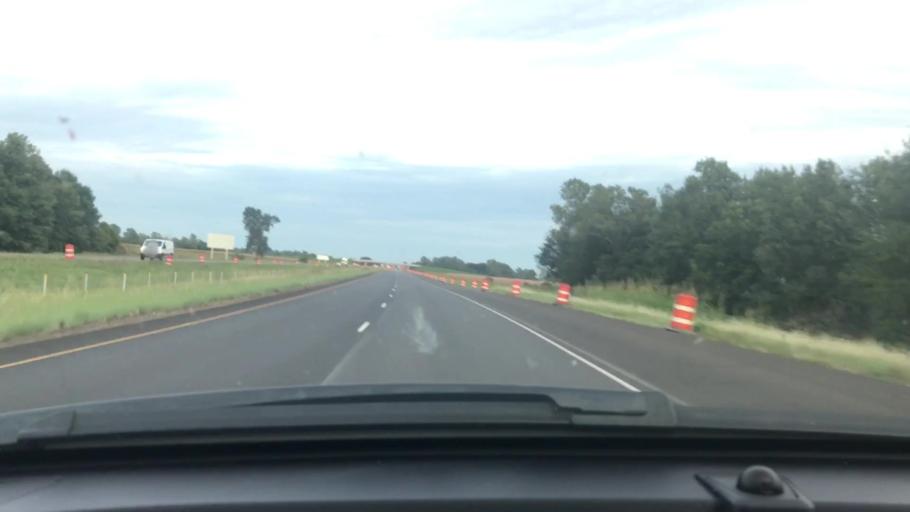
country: US
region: Arkansas
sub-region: Poinsett County
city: Trumann
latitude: 35.6586
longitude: -90.5456
